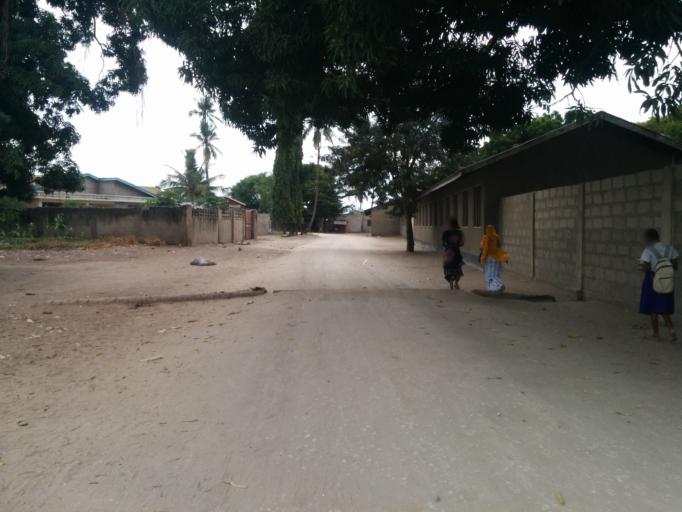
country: TZ
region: Dar es Salaam
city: Dar es Salaam
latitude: -6.8745
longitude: 39.2463
